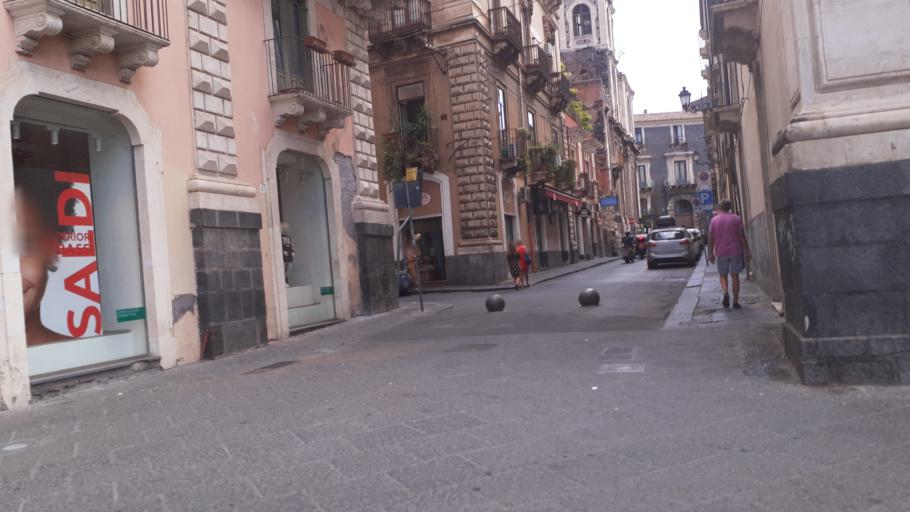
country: IT
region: Sicily
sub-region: Catania
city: Catania
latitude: 37.5039
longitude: 15.0874
